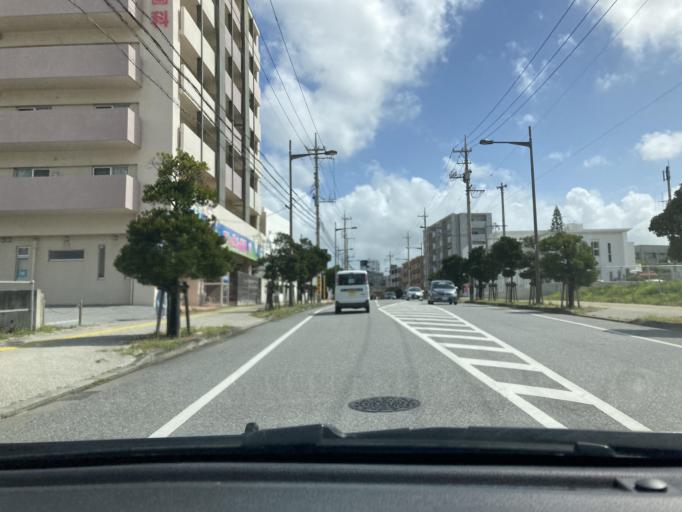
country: JP
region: Okinawa
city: Ginowan
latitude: 26.2718
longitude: 127.7308
